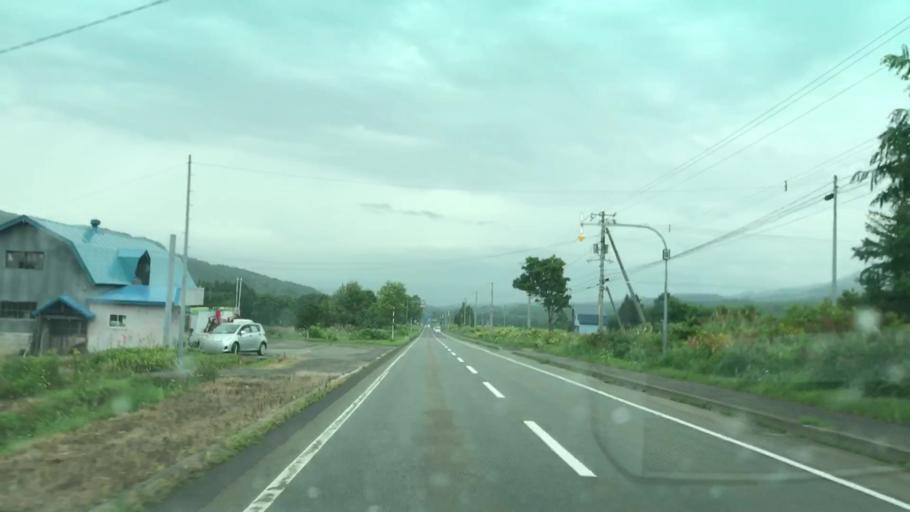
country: JP
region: Hokkaido
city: Niseko Town
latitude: 42.7645
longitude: 140.4819
